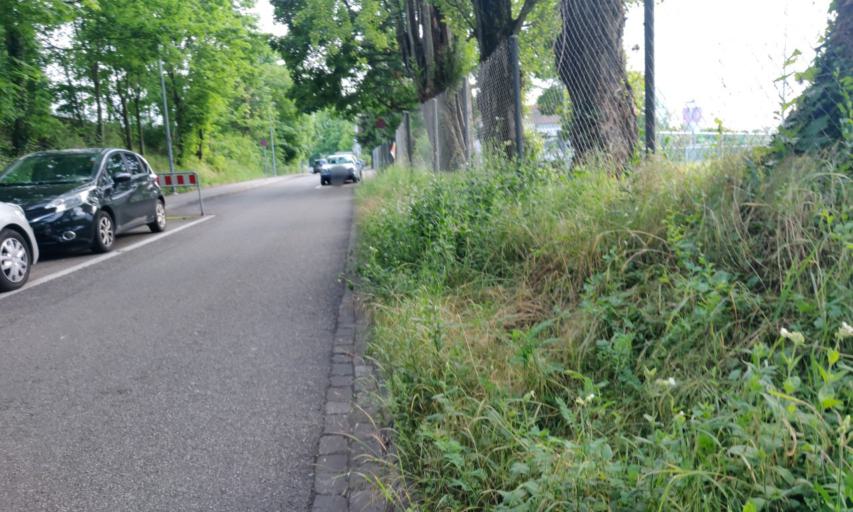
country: CH
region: Basel-Landschaft
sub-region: Bezirk Arlesheim
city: Birsfelden
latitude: 47.5648
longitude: 7.6290
